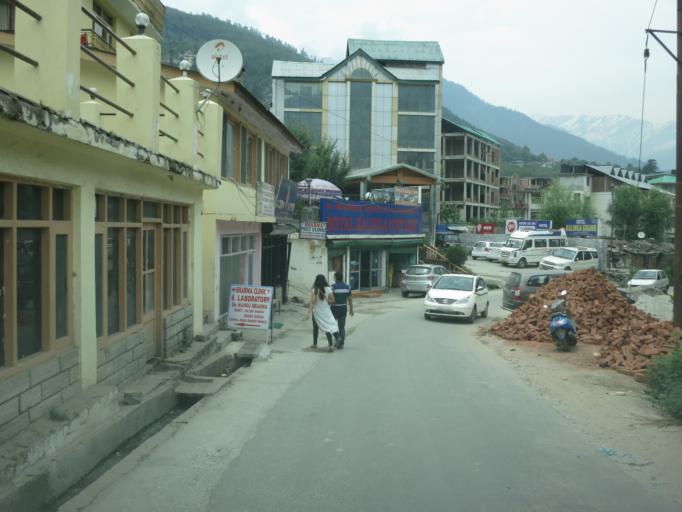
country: IN
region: Himachal Pradesh
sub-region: Kulu
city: Manali
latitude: 32.2223
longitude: 77.1900
